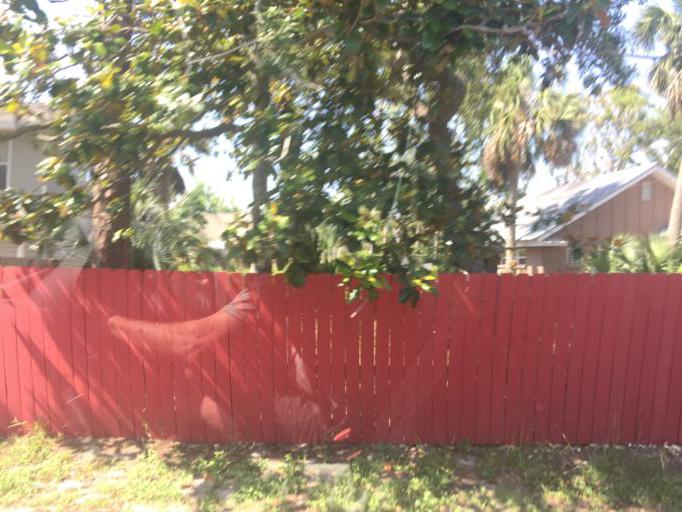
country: US
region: Florida
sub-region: Bay County
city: Upper Grand Lagoon
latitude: 30.1570
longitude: -85.7250
